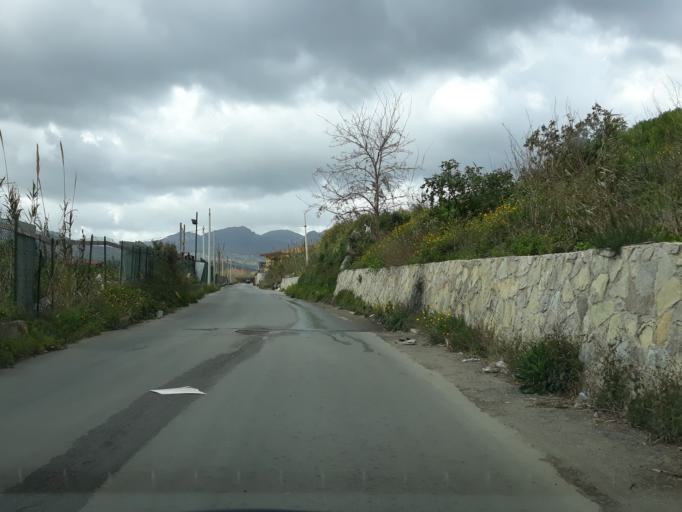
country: IT
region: Sicily
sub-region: Palermo
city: Monreale
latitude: 38.0799
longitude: 13.2939
